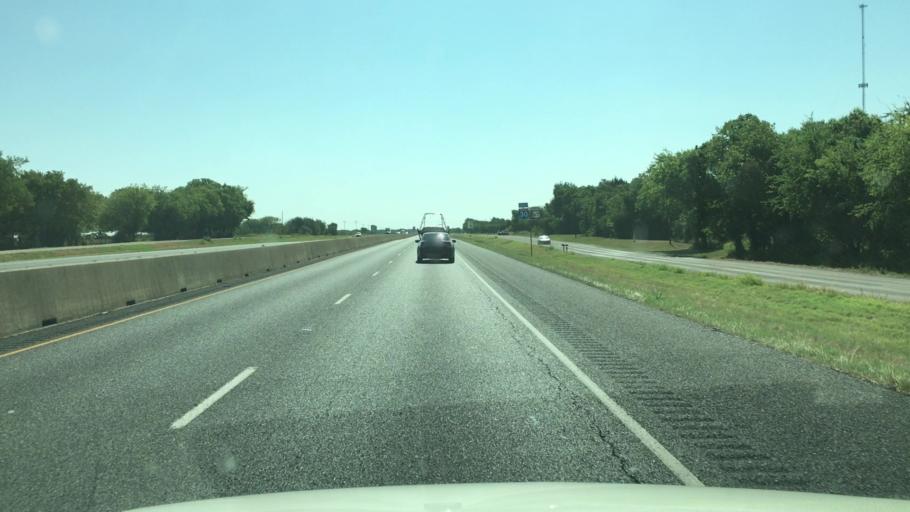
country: US
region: Texas
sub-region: Hunt County
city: Commerce
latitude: 33.1316
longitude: -95.9310
